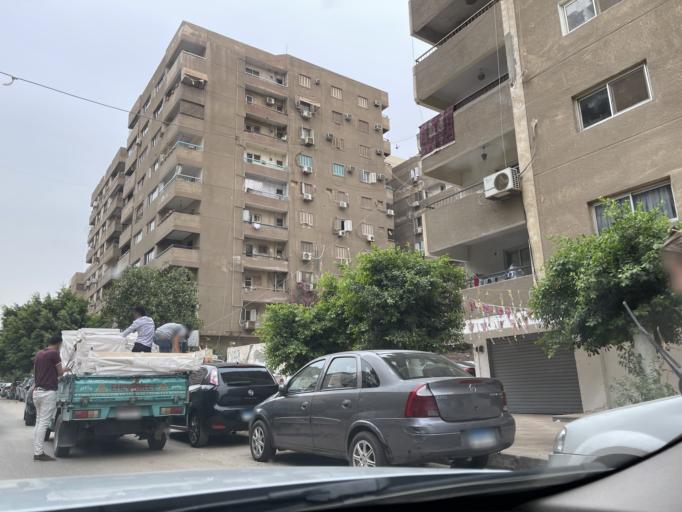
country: EG
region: Muhafazat al Qahirah
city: Cairo
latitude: 30.0605
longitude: 31.3550
